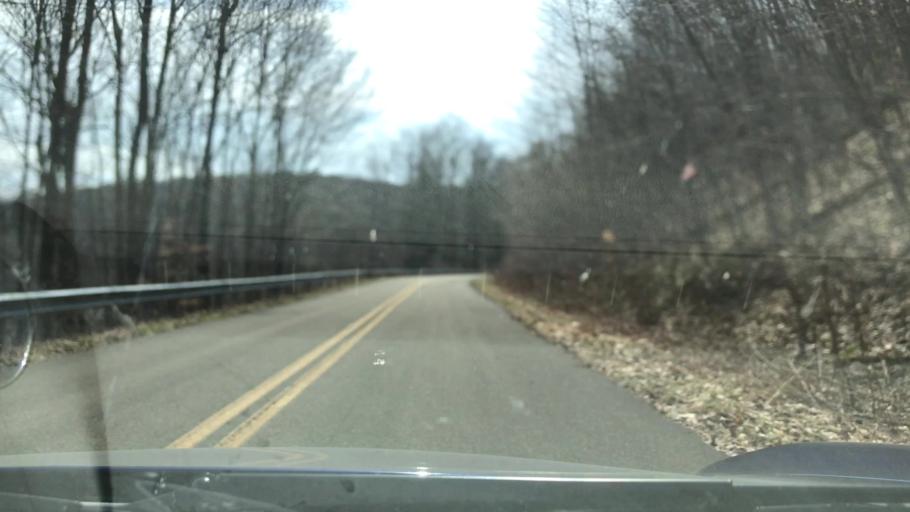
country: US
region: Pennsylvania
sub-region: Warren County
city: Sheffield
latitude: 41.8190
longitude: -78.9494
